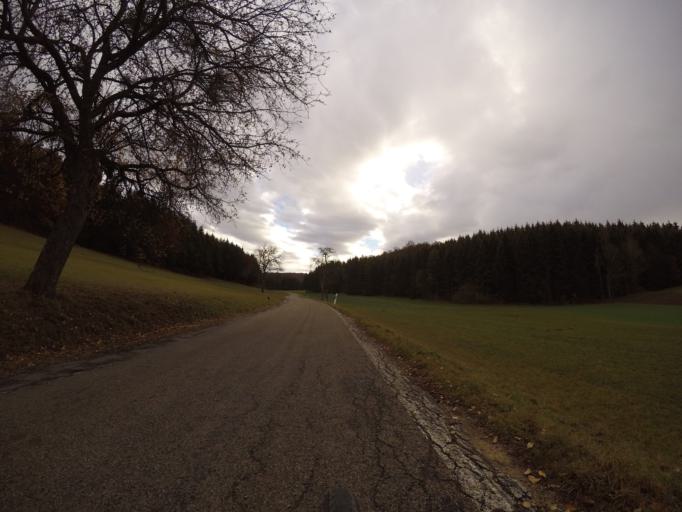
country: DE
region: Baden-Wuerttemberg
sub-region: Tuebingen Region
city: Sankt Johann
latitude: 48.4141
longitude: 9.2922
